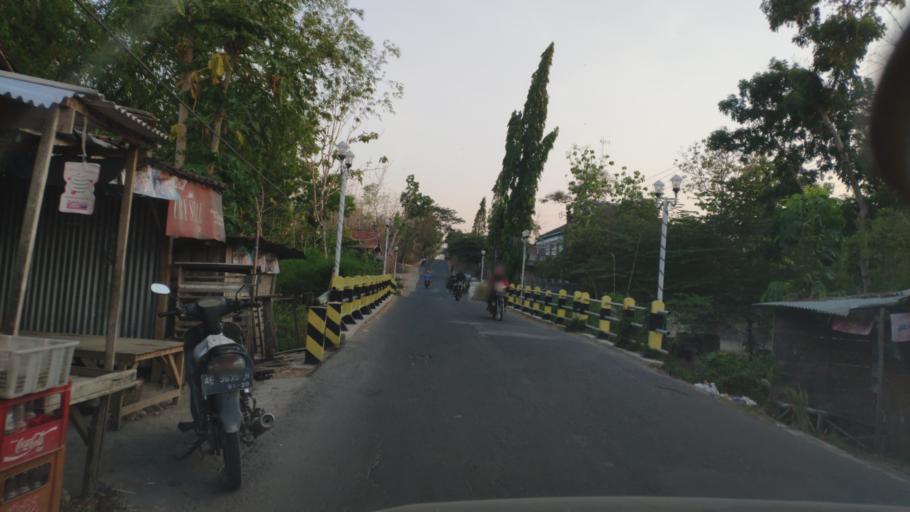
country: ID
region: Central Java
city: Badong
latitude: -7.0053
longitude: 111.4101
